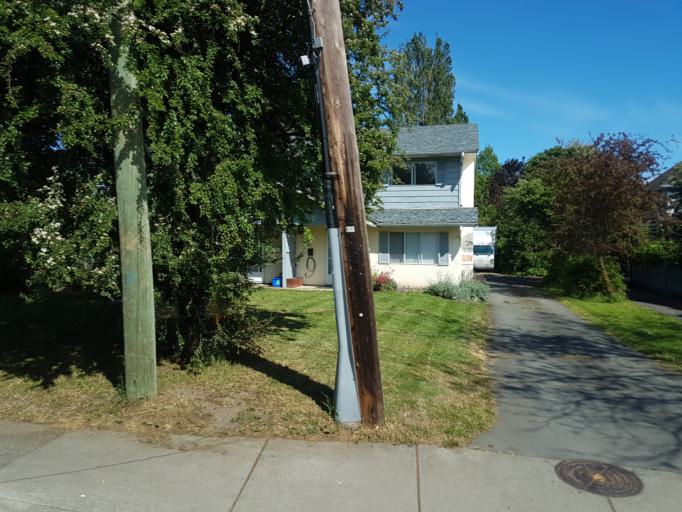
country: CA
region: British Columbia
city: Oak Bay
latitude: 48.4809
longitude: -123.3229
